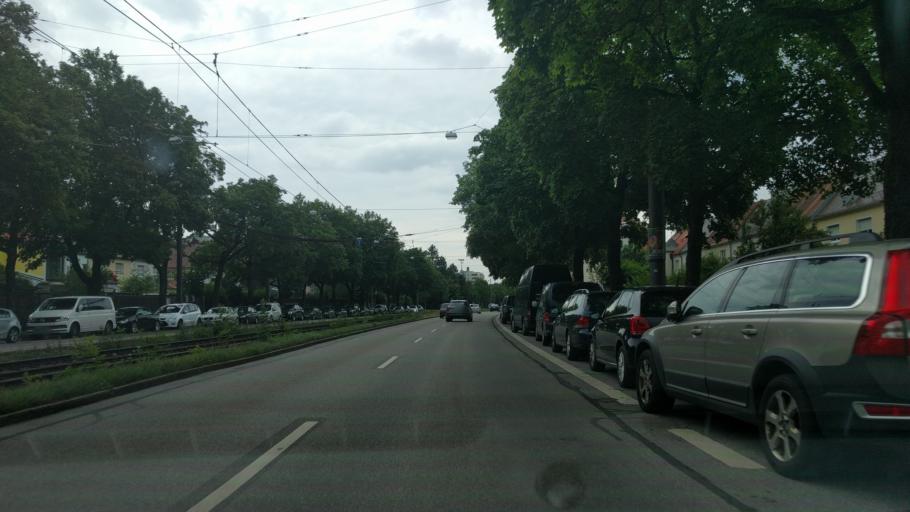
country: DE
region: Bavaria
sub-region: Upper Bavaria
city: Munich
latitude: 48.0969
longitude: 11.5641
